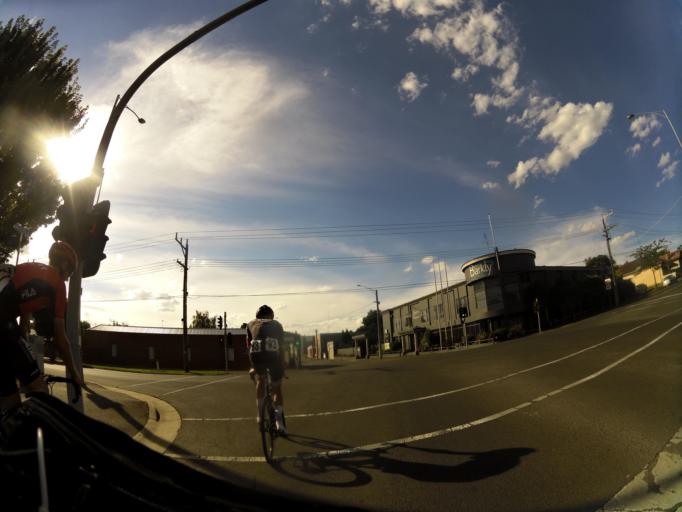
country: AU
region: Victoria
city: Ballarat East
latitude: -37.5652
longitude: 143.8675
